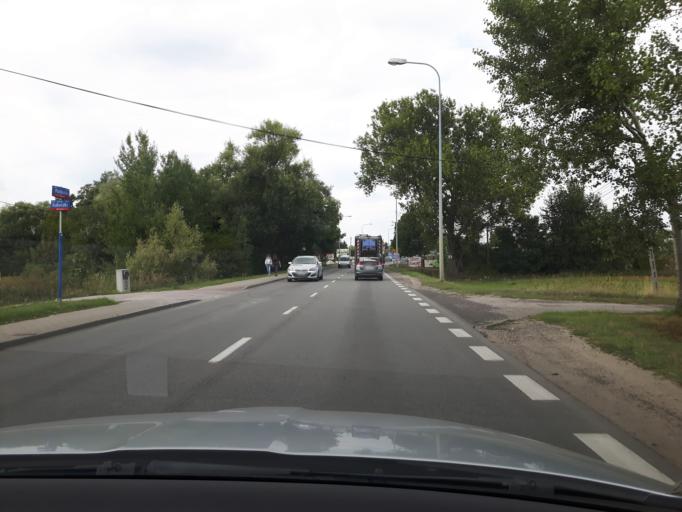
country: PL
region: Masovian Voivodeship
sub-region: Powiat legionowski
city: Stanislawow Pierwszy
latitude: 52.3532
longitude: 21.0289
